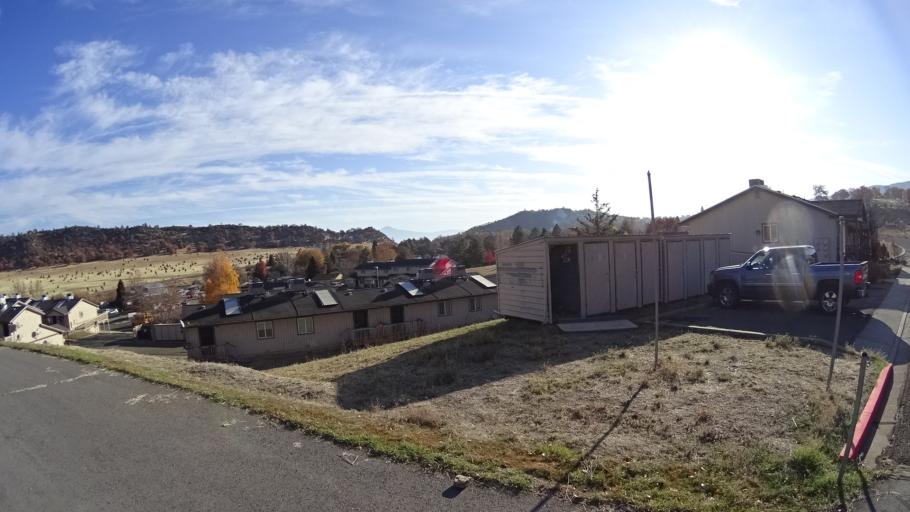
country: US
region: California
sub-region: Siskiyou County
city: Yreka
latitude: 41.7121
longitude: -122.6265
